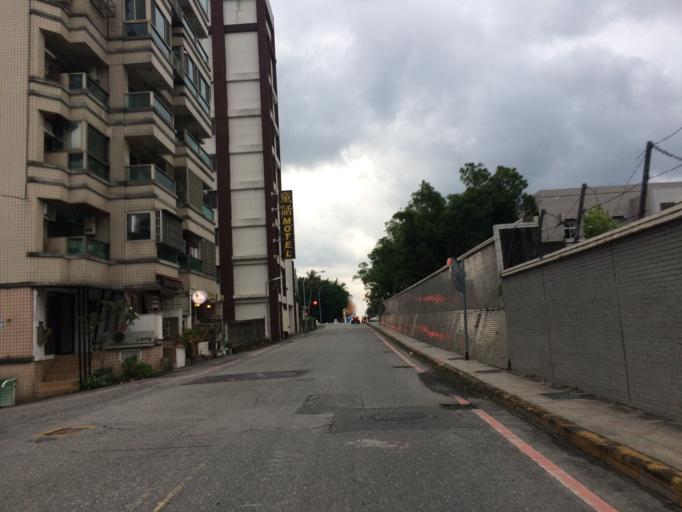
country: TW
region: Taiwan
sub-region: Hualien
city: Hualian
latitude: 23.9798
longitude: 121.6163
